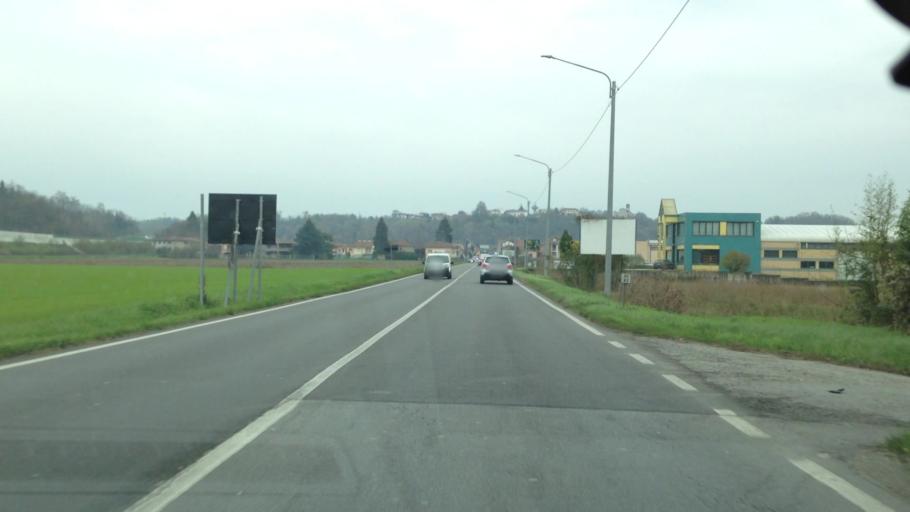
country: IT
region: Piedmont
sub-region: Provincia di Asti
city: Azzano d'Asti
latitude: 44.9073
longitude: 8.2755
